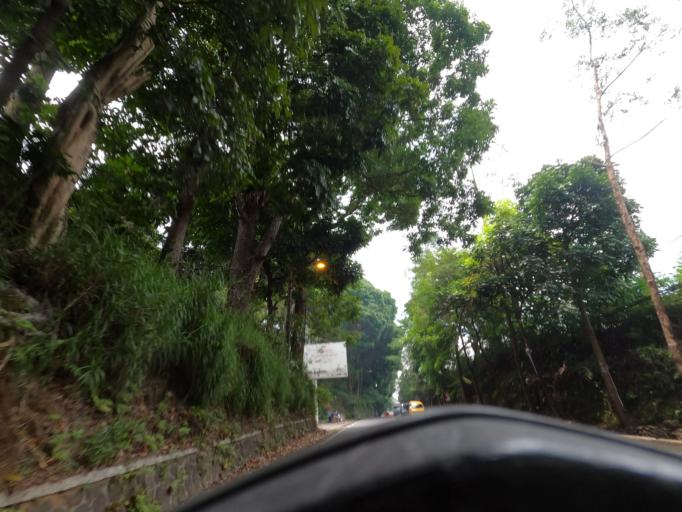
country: ID
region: West Java
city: Sukabumi
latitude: -6.7573
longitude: 107.0468
